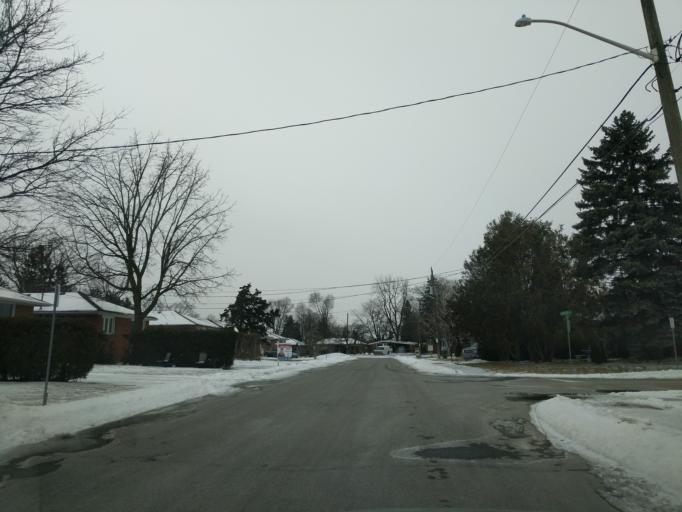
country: CA
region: Ontario
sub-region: York
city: Richmond Hill
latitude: 43.8777
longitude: -79.4184
